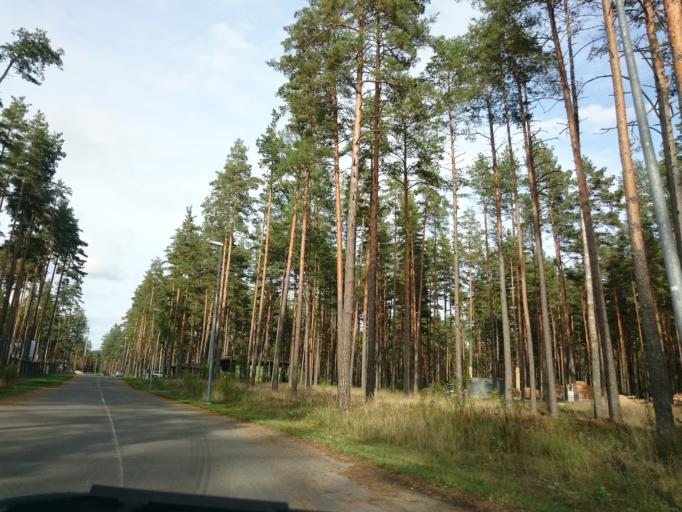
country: LV
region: Adazi
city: Adazi
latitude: 57.0528
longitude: 24.3599
